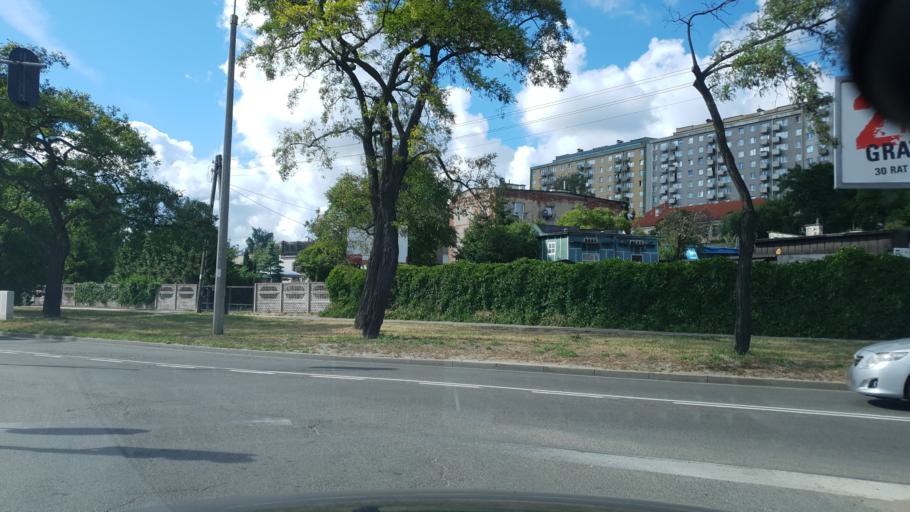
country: PL
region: Pomeranian Voivodeship
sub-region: Gdynia
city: Gdynia
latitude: 54.5485
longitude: 18.5169
